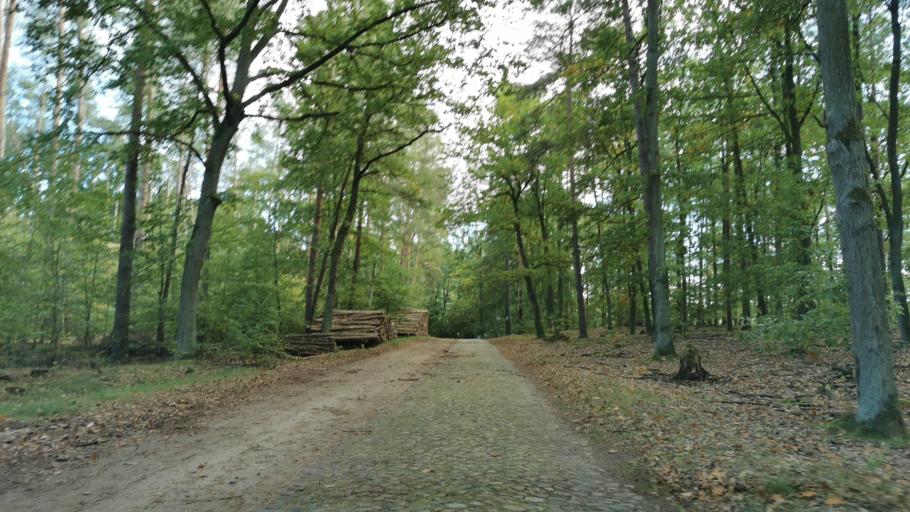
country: DE
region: Brandenburg
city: Michendorf
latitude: 52.3137
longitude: 12.9725
